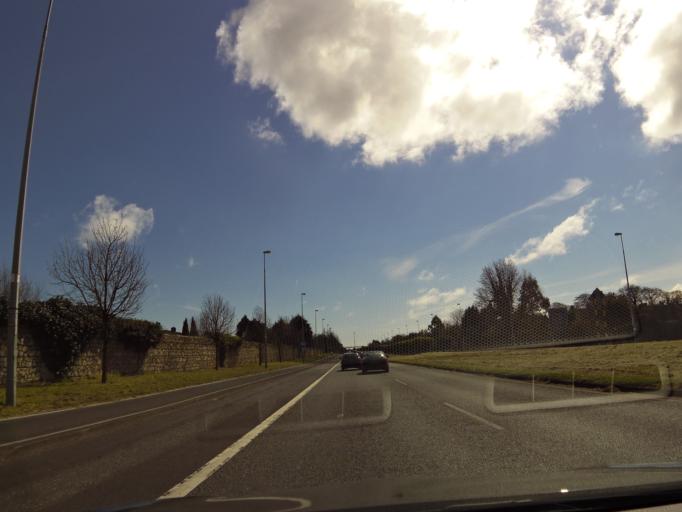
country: IE
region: Leinster
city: Cabinteely
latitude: 53.2658
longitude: -6.1569
